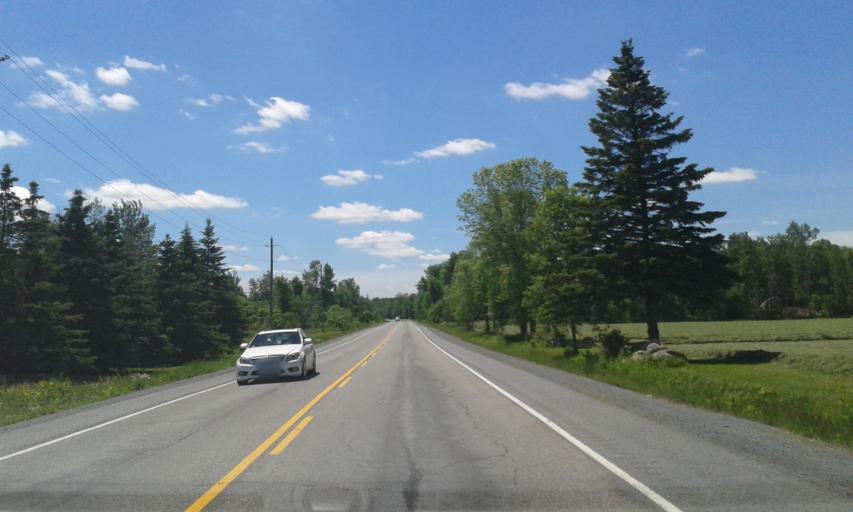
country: CA
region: Ontario
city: Cornwall
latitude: 45.1211
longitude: -74.5091
